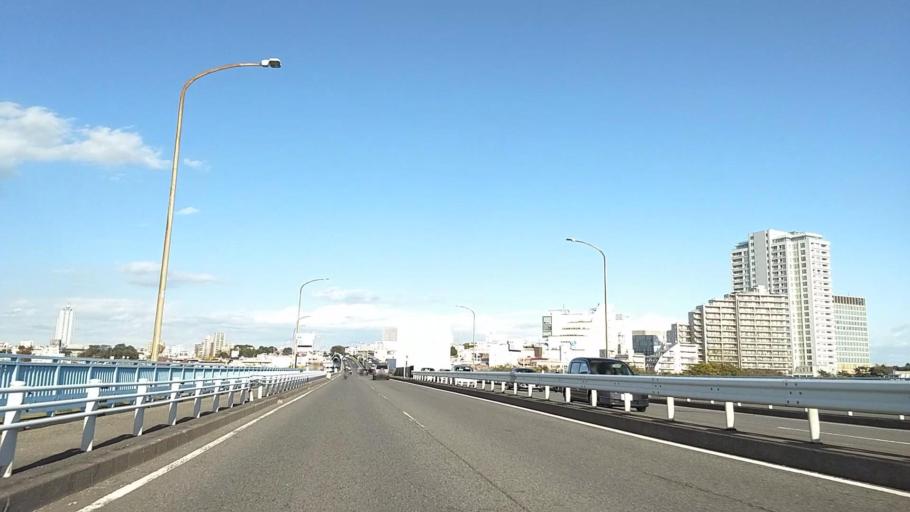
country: JP
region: Tokyo
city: Chofugaoka
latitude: 35.6112
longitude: 139.6211
